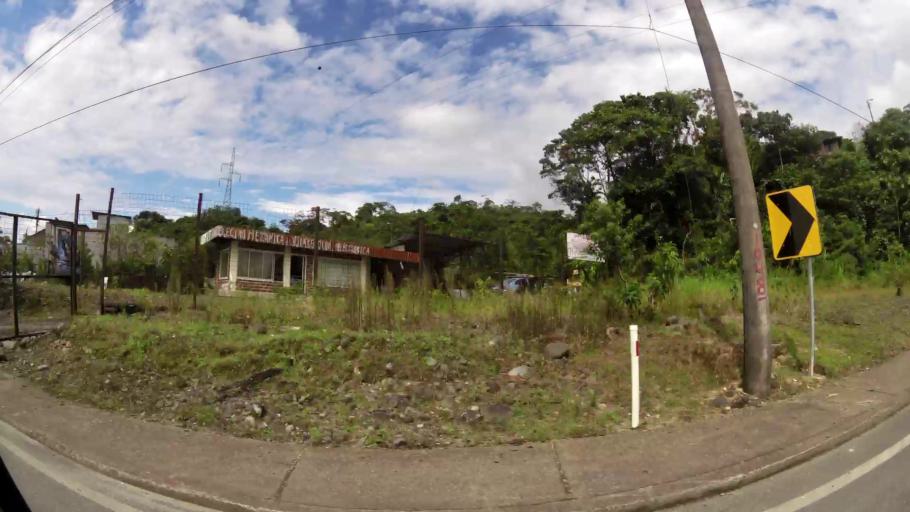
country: EC
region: Pastaza
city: Puyo
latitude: -1.4934
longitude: -78.0183
